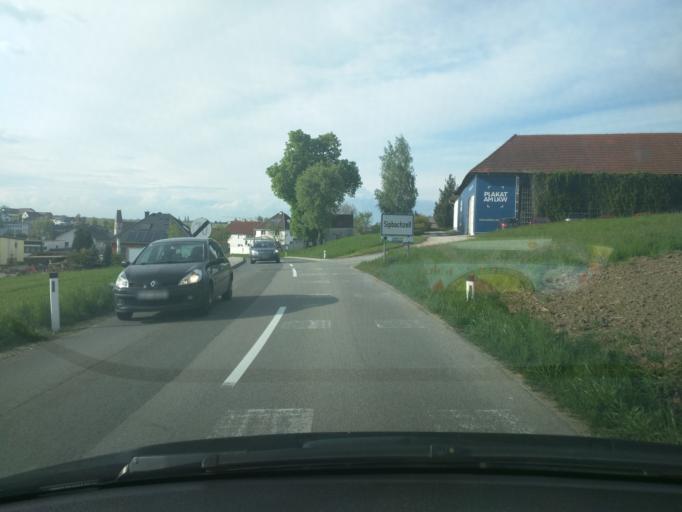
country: AT
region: Upper Austria
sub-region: Politischer Bezirk Kirchdorf an der Krems
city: Kremsmunster
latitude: 48.0926
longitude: 14.1113
